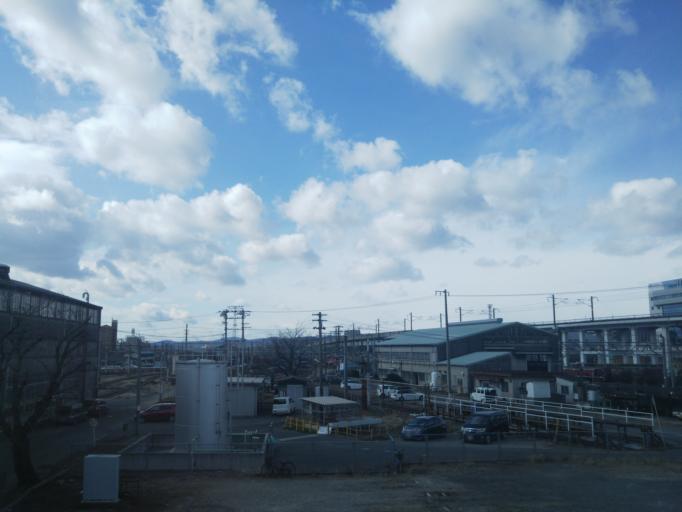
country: JP
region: Okayama
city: Okayama-shi
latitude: 34.6549
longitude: 133.9105
